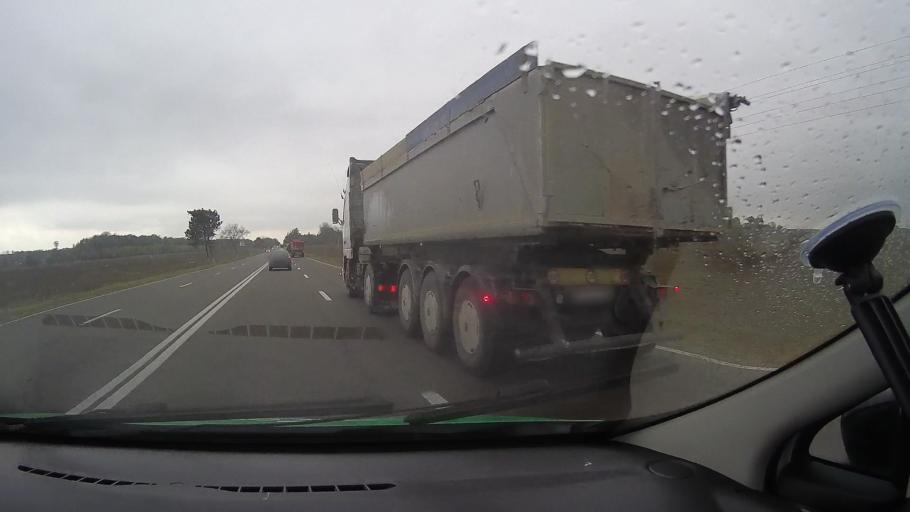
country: RO
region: Constanta
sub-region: Comuna Valu lui Traian
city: Valu lui Traian
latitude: 44.1656
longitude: 28.5175
